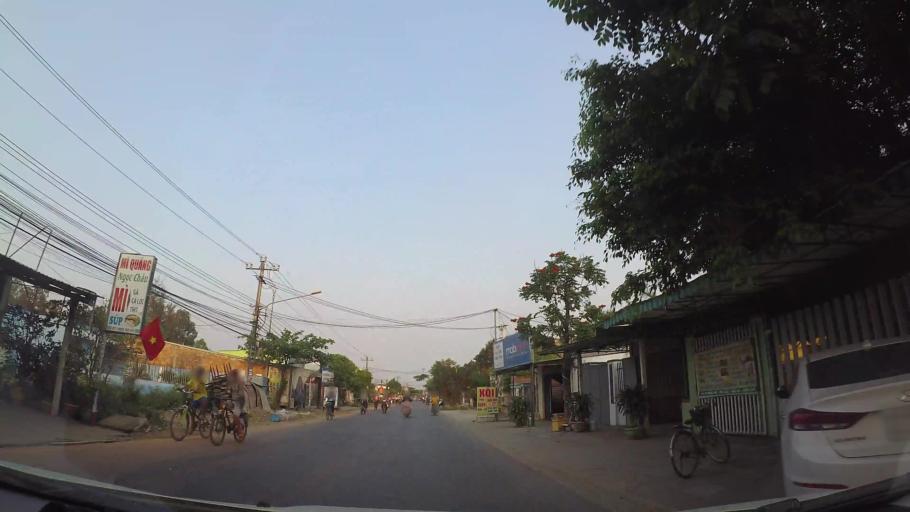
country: VN
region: Da Nang
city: Ngu Hanh Son
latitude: 15.9559
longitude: 108.2514
